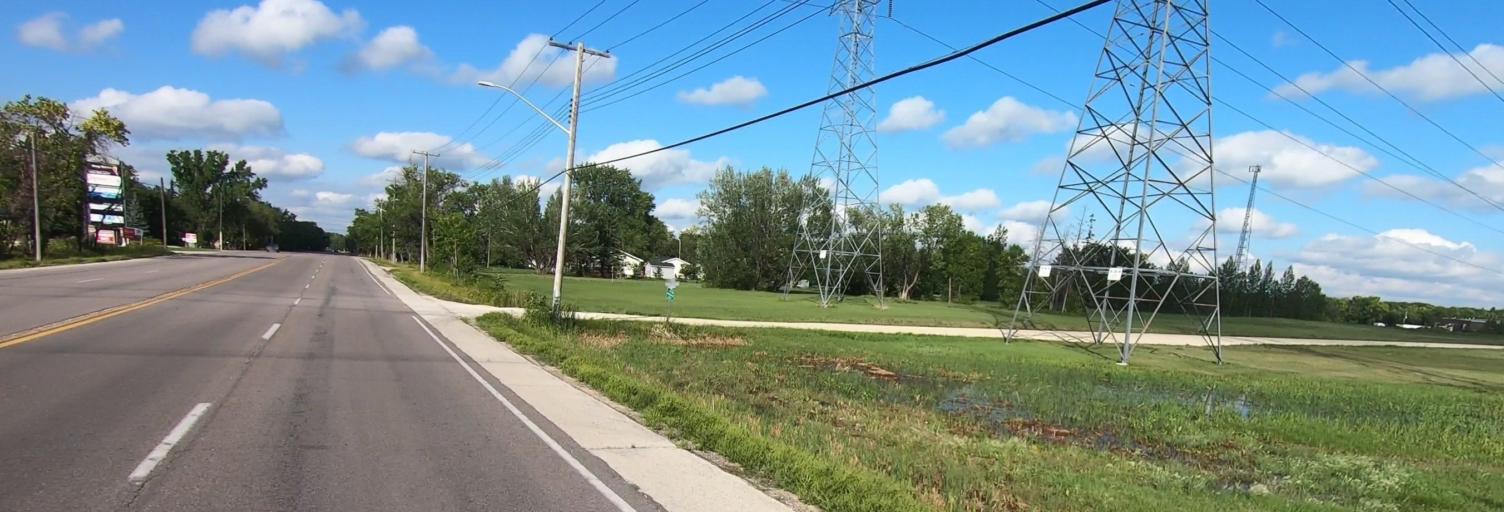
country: CA
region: Manitoba
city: Winnipeg
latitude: 49.9852
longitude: -97.0467
